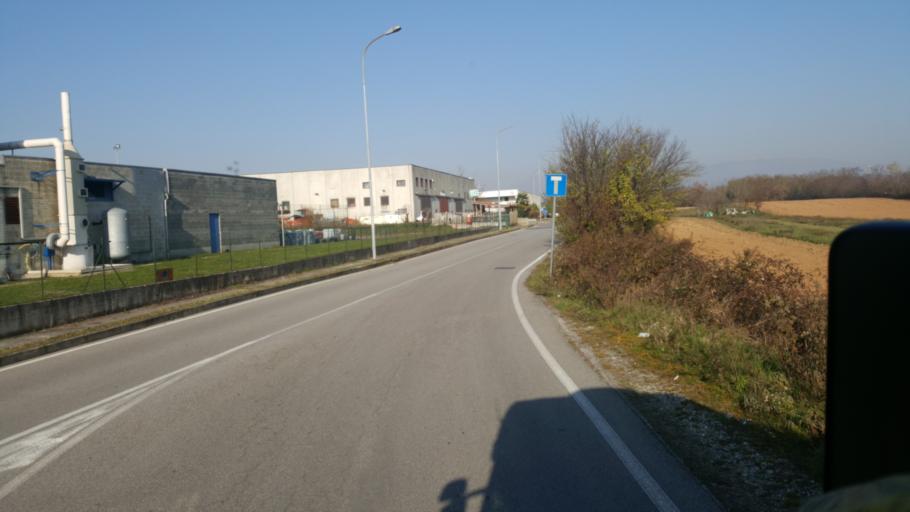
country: IT
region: Lombardy
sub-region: Provincia di Monza e Brianza
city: Bellusco
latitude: 45.6245
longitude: 9.4305
